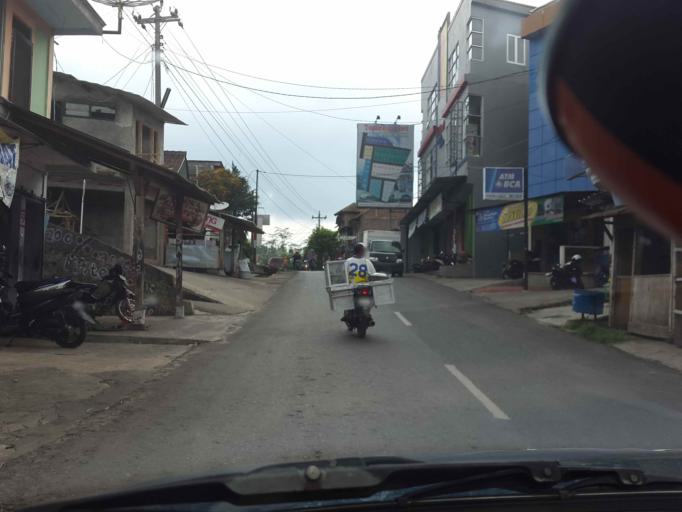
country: ID
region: Central Java
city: Gunung Kendil
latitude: -7.3721
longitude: 110.3255
